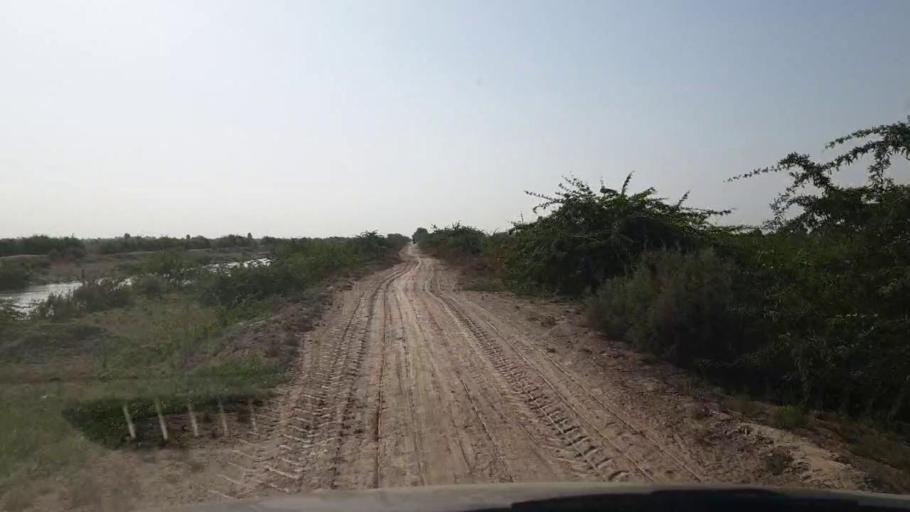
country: PK
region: Sindh
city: Kadhan
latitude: 24.5911
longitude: 69.0766
